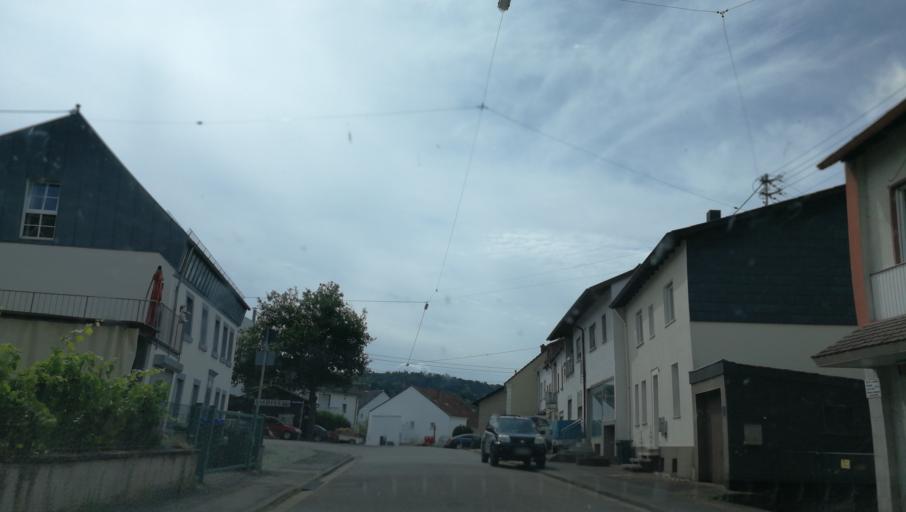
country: DE
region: Saarland
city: Merzig
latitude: 49.4701
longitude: 6.6757
